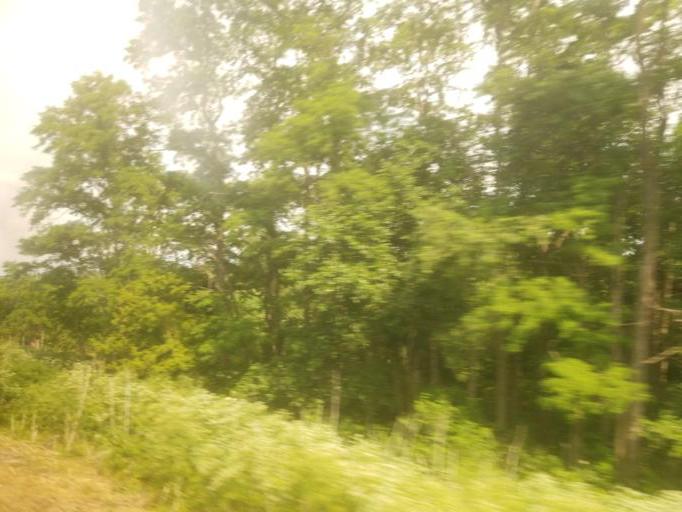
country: US
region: Illinois
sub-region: Knox County
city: Galesburg
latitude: 40.9071
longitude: -90.4324
